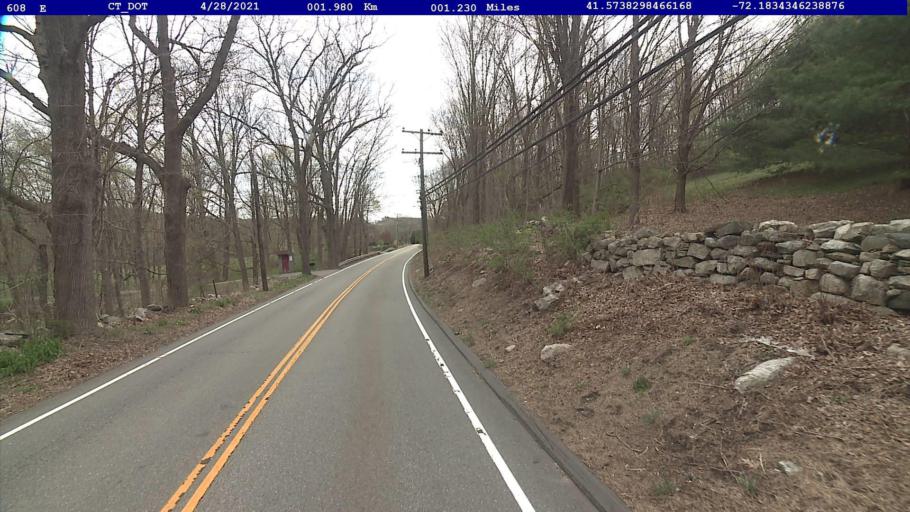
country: US
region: Connecticut
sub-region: New London County
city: Montville Center
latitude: 41.5736
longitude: -72.1835
